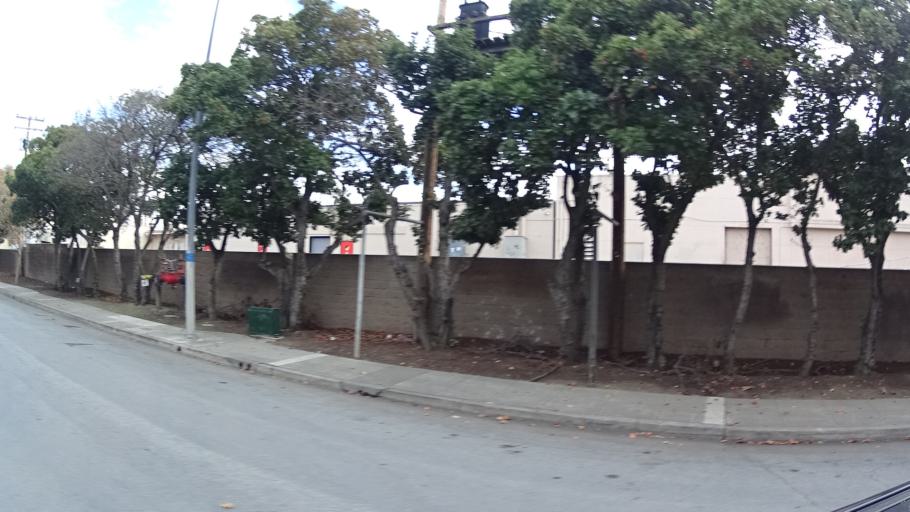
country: US
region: California
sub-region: Santa Clara County
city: Buena Vista
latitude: 37.3244
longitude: -121.9226
